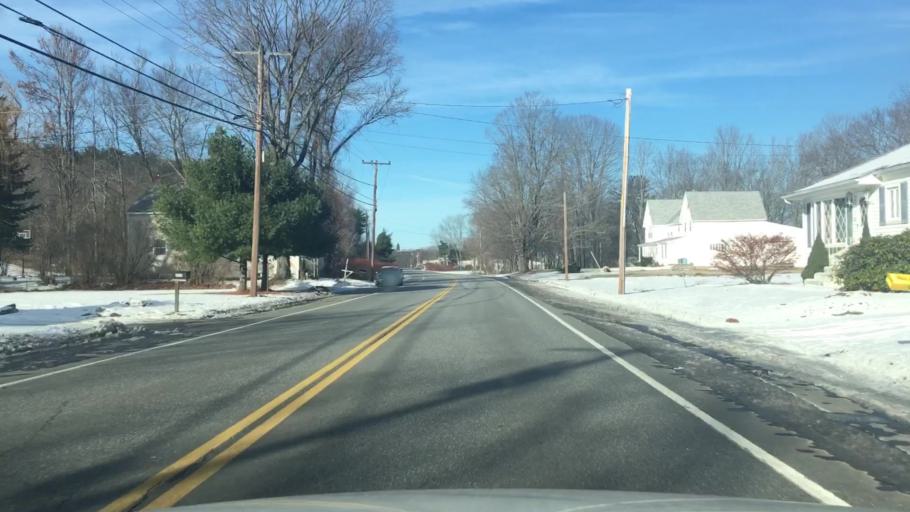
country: US
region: Maine
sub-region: Androscoggin County
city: Lewiston
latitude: 44.0738
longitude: -70.2091
